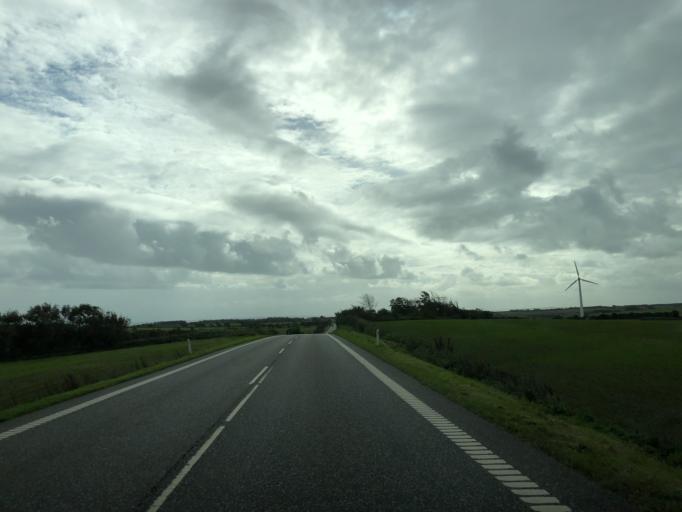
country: DK
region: North Denmark
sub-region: Thisted Kommune
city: Hurup
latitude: 56.7049
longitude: 8.4115
